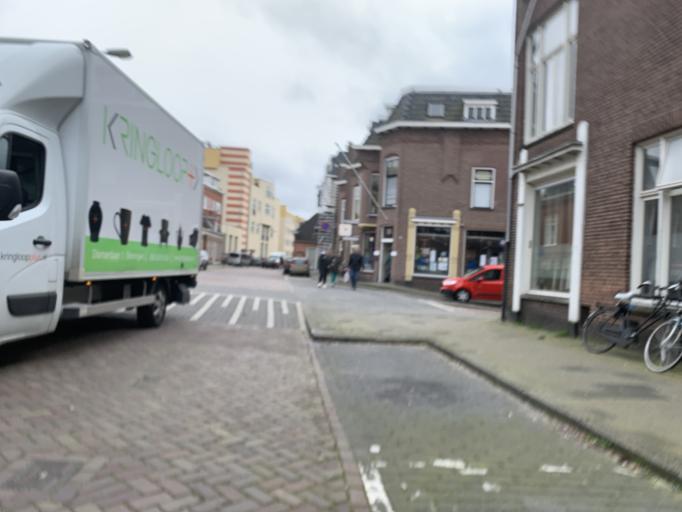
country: NL
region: Groningen
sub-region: Gemeente Groningen
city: Korrewegwijk
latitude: 53.2277
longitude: 6.5554
